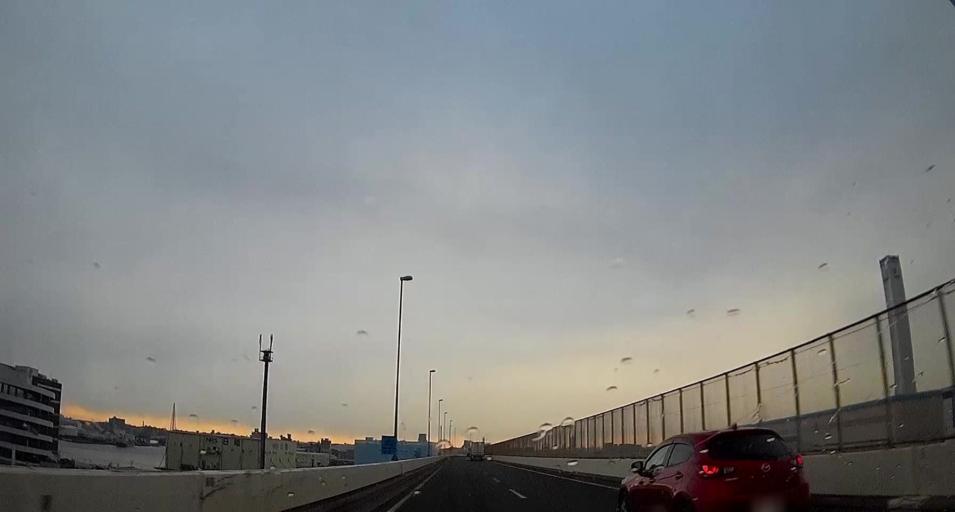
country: JP
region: Kanagawa
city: Yokohama
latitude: 35.4729
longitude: 139.6748
